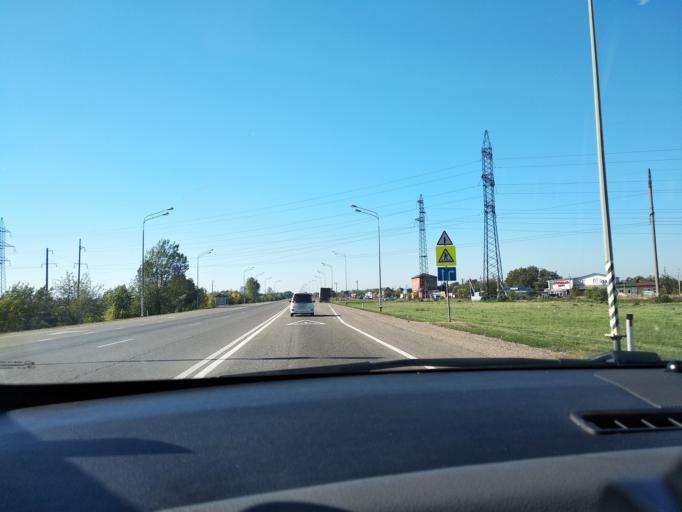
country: RU
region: Krasnodarskiy
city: Agronom
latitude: 45.1597
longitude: 39.0777
